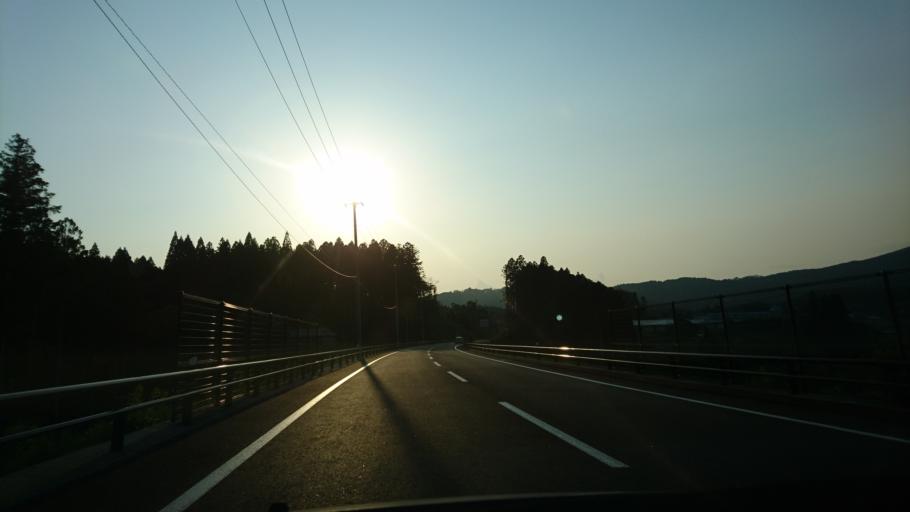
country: JP
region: Iwate
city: Ofunato
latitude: 38.9322
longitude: 141.4440
